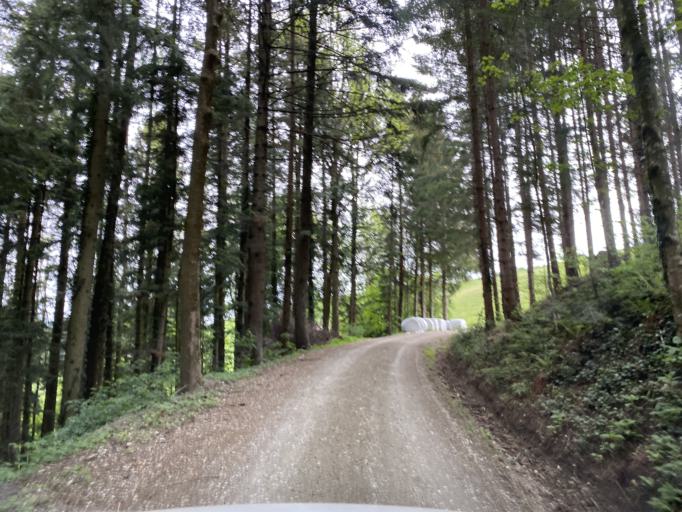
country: AT
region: Styria
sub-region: Politischer Bezirk Weiz
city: Koglhof
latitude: 47.3214
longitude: 15.6840
